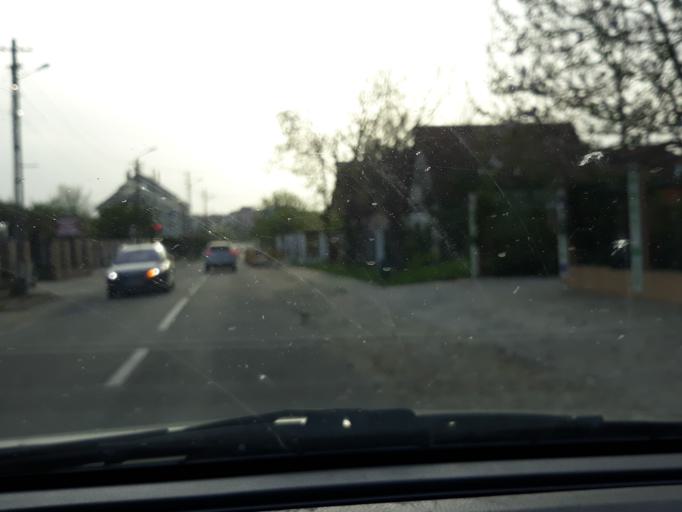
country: RO
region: Bihor
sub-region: Comuna Sanmartin
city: Sanmartin
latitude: 47.0012
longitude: 21.9868
